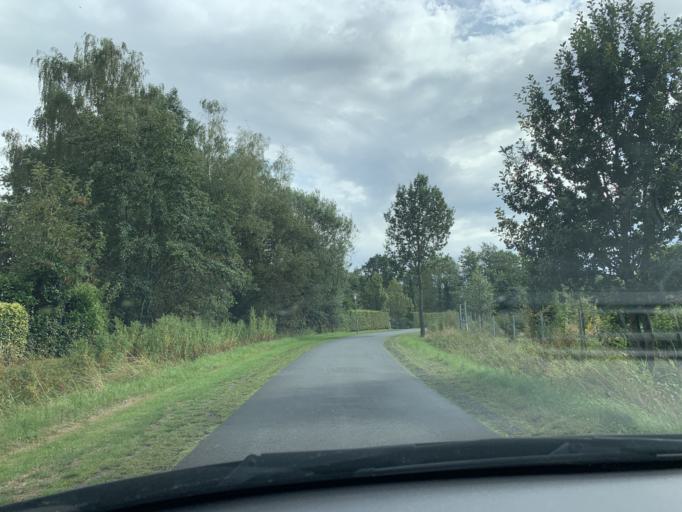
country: DE
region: Lower Saxony
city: Westerstede
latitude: 53.2658
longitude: 7.9001
